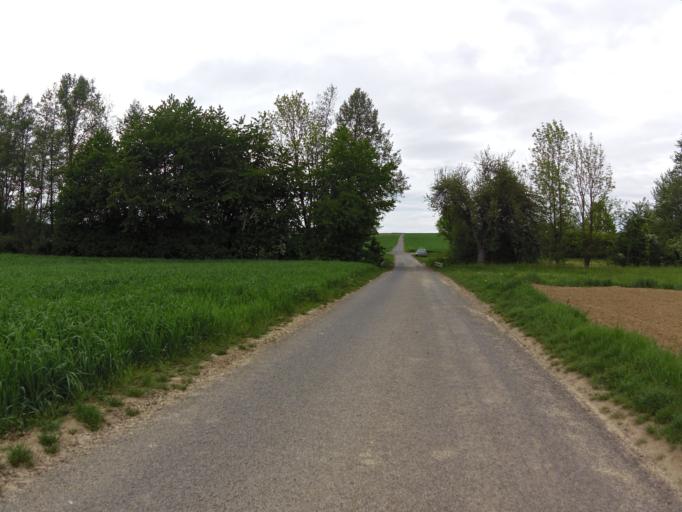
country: DE
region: Bavaria
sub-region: Regierungsbezirk Unterfranken
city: Kurnach
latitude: 49.8467
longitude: 10.0608
